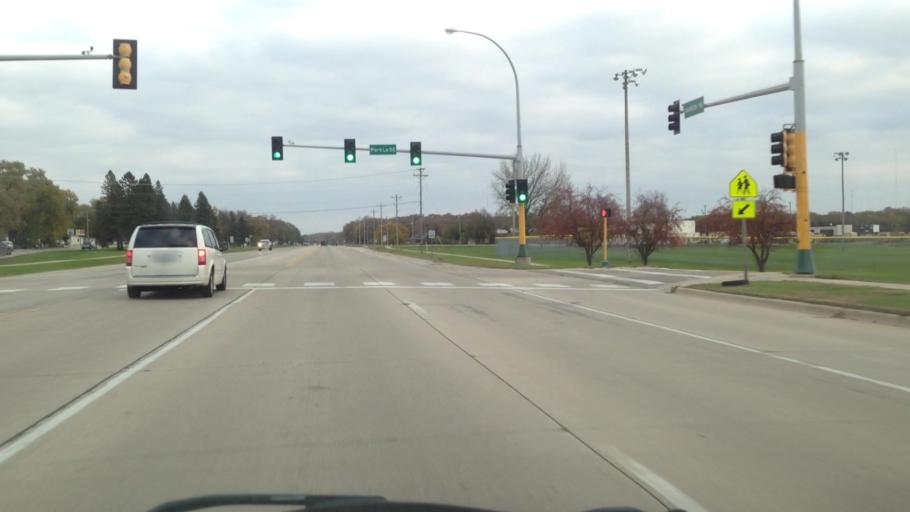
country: US
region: Minnesota
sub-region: Olmsted County
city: Rochester
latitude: 43.9995
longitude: -92.4336
